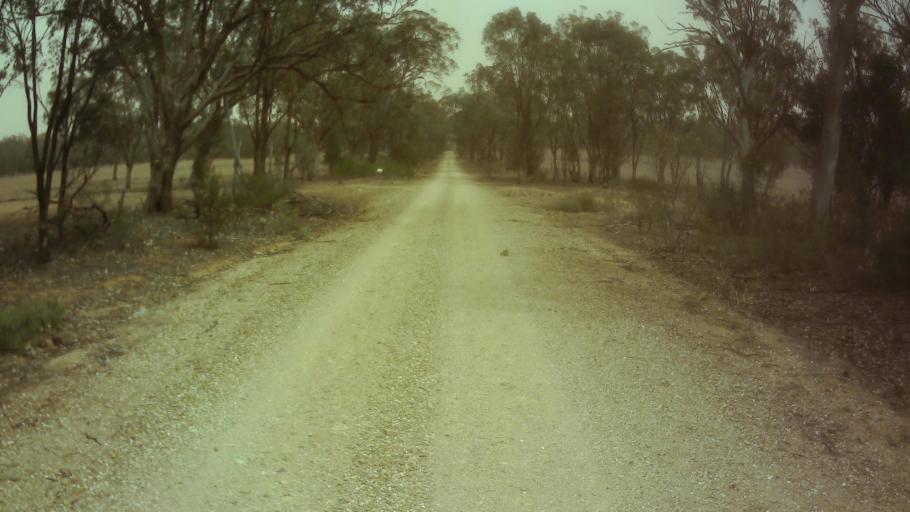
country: AU
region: New South Wales
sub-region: Weddin
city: Grenfell
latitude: -33.7100
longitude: 147.9530
